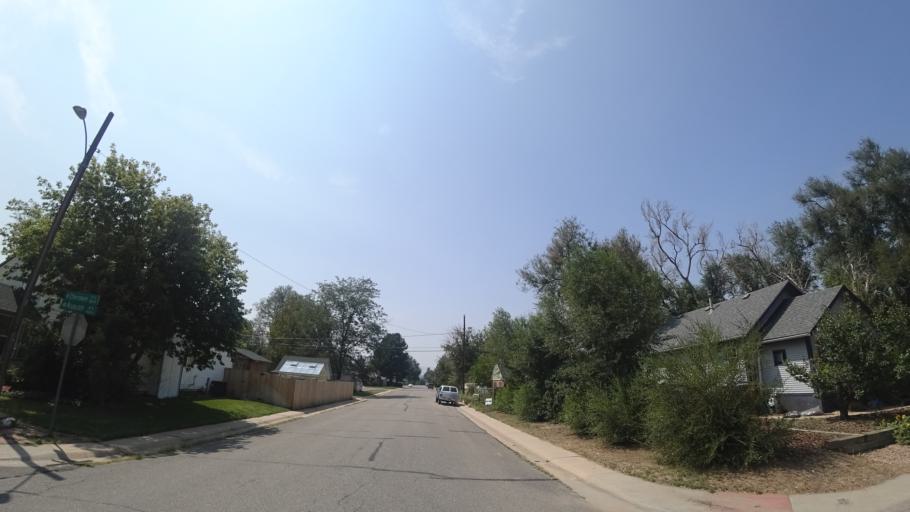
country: US
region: Colorado
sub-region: Arapahoe County
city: Englewood
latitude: 39.6368
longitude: -104.9914
